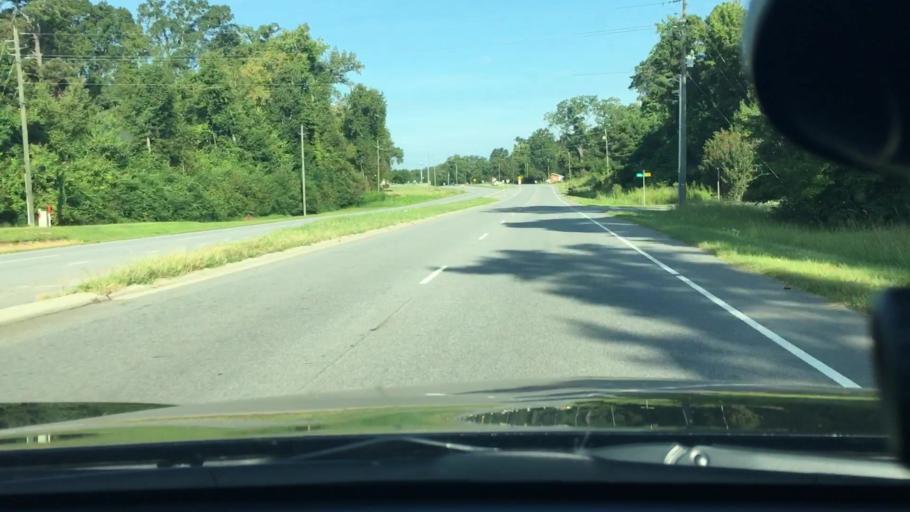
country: US
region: North Carolina
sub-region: Pitt County
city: Greenville
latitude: 35.6265
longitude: -77.4251
